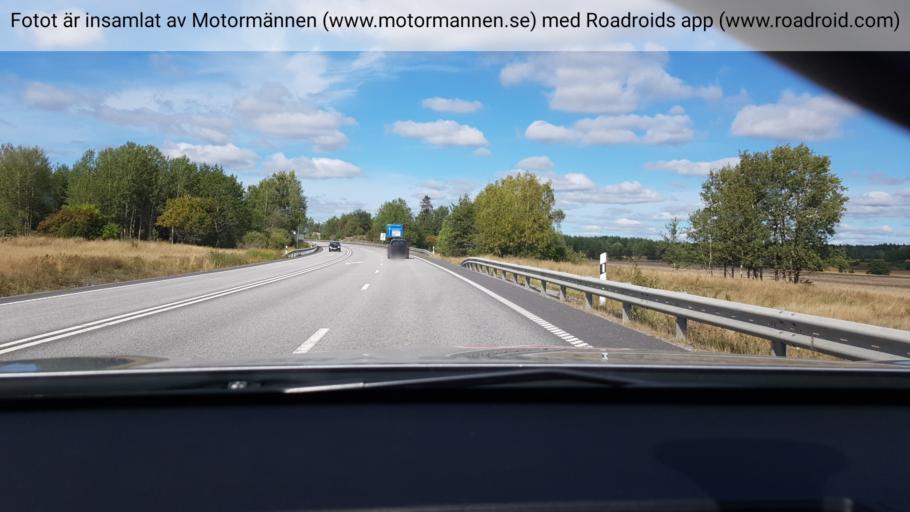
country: SE
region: Stockholm
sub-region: Osterakers Kommun
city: Akersberga
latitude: 59.4459
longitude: 18.2215
